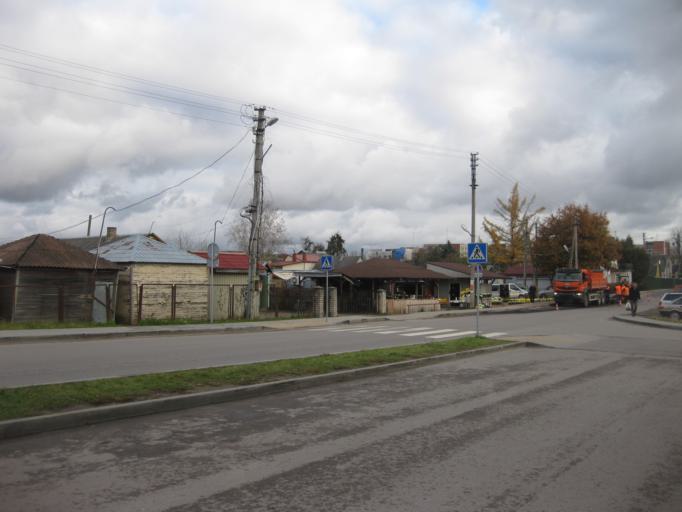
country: LT
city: Prienai
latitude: 54.6432
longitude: 23.9449
